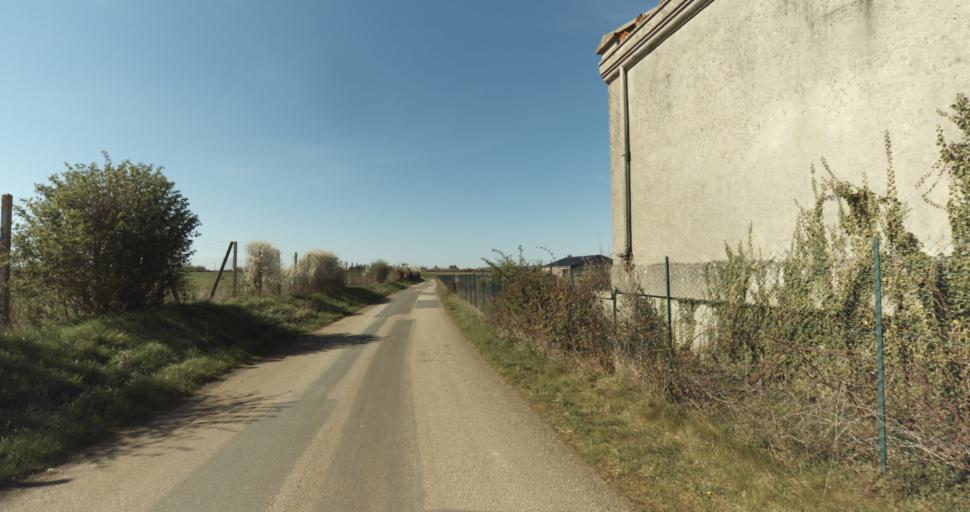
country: FR
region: Lower Normandy
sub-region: Departement du Calvados
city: Saint-Pierre-sur-Dives
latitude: 49.0485
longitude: -0.0508
